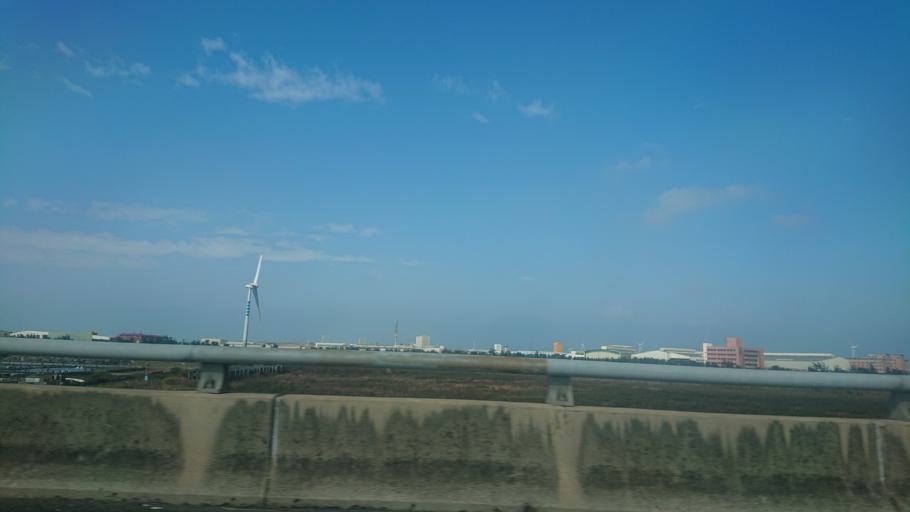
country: TW
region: Taiwan
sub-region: Changhua
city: Chang-hua
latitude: 24.0702
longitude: 120.4139
